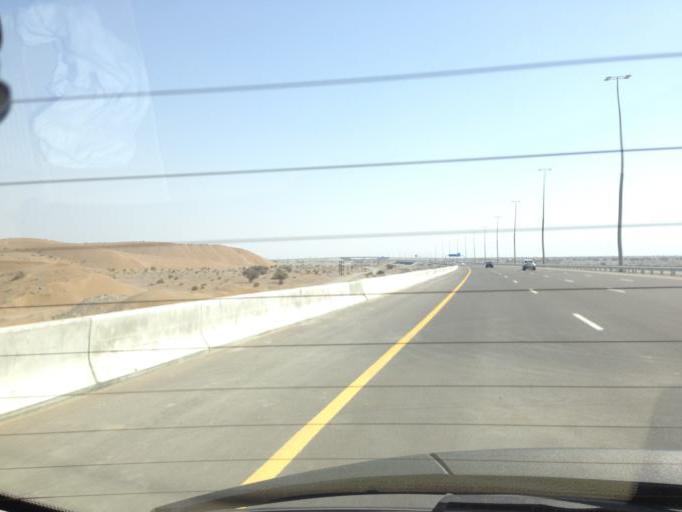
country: OM
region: Al Batinah
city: Bayt al `Awabi
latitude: 23.5195
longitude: 57.6453
